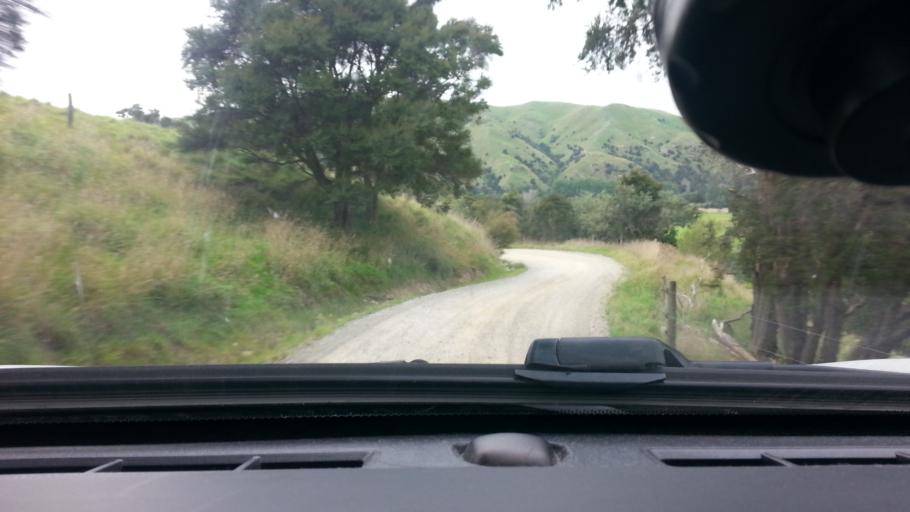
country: NZ
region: Wellington
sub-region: Masterton District
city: Masterton
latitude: -41.1492
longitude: 175.4774
